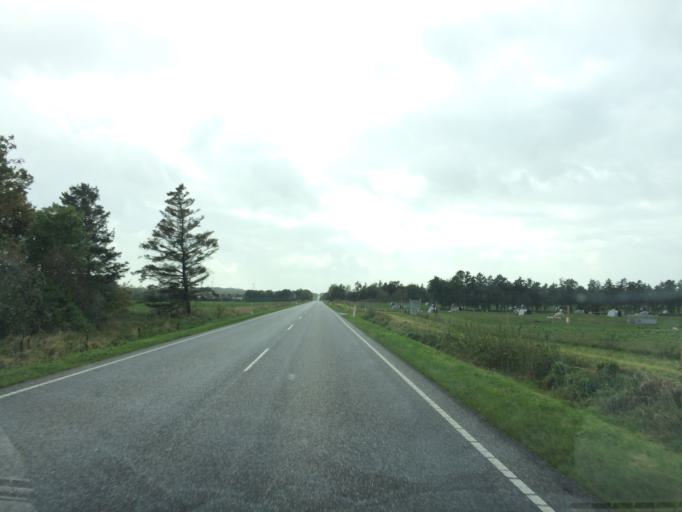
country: DK
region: Central Jutland
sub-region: Holstebro Kommune
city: Holstebro
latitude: 56.3445
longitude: 8.5490
